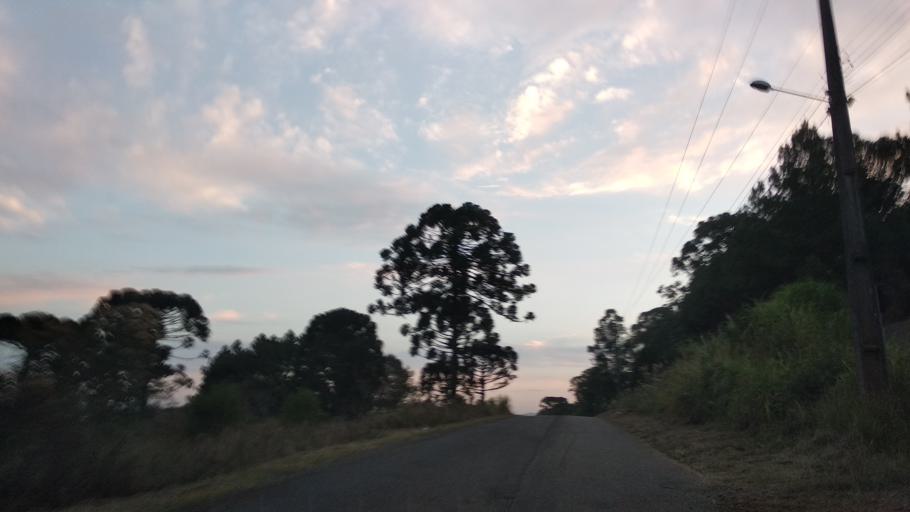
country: BR
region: Santa Catarina
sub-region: Videira
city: Videira
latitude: -26.9969
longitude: -51.1826
